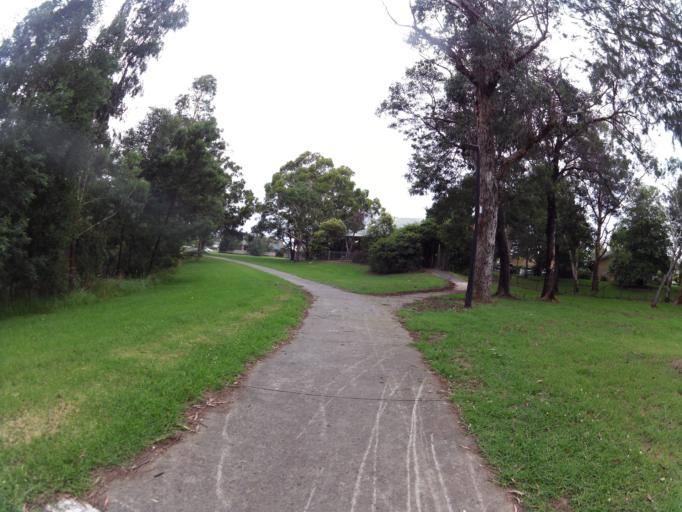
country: AU
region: Victoria
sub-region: Latrobe
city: Traralgon
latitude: -38.1997
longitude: 146.5408
